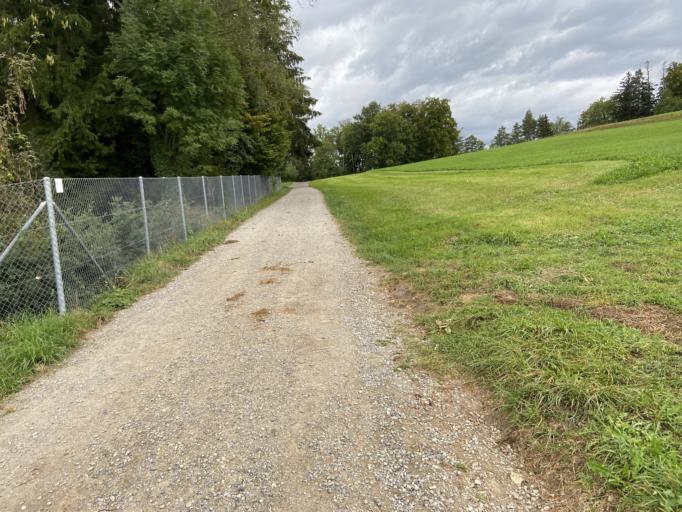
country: CH
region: Zurich
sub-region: Bezirk Meilen
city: Stafa
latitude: 47.2559
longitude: 8.7219
